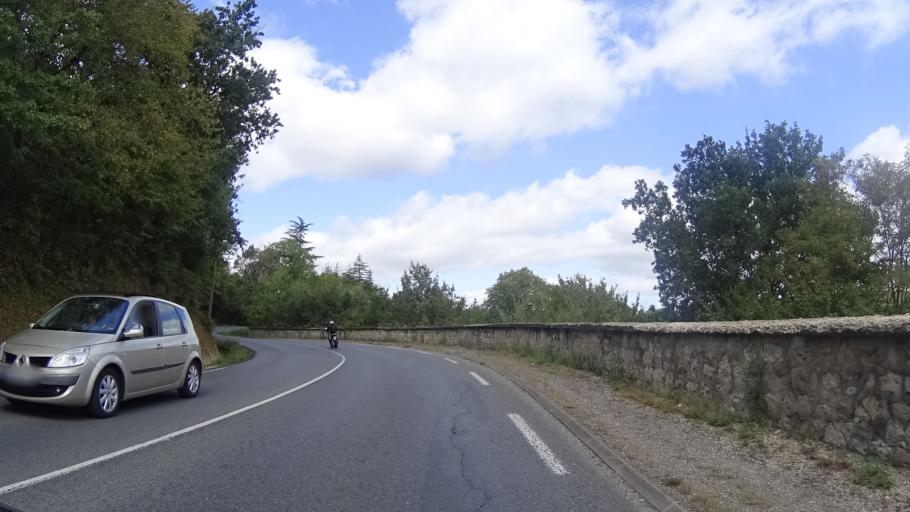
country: FR
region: Aquitaine
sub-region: Departement du Lot-et-Garonne
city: Agen
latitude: 44.2166
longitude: 0.6395
